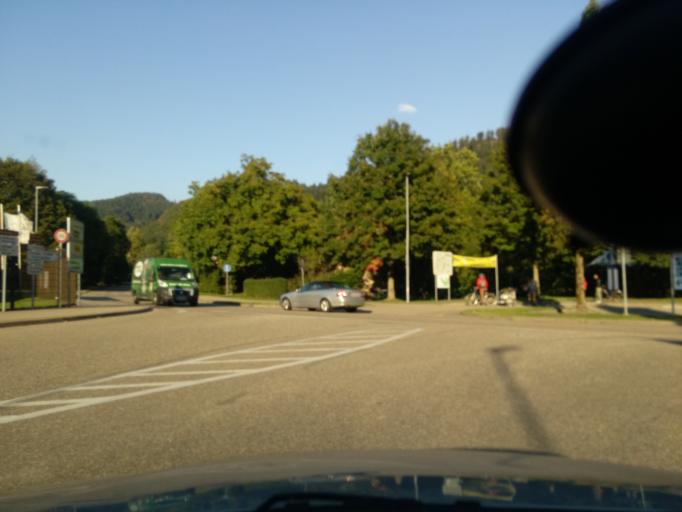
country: DE
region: Baden-Wuerttemberg
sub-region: Freiburg Region
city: Wolfach
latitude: 48.2897
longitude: 8.2156
